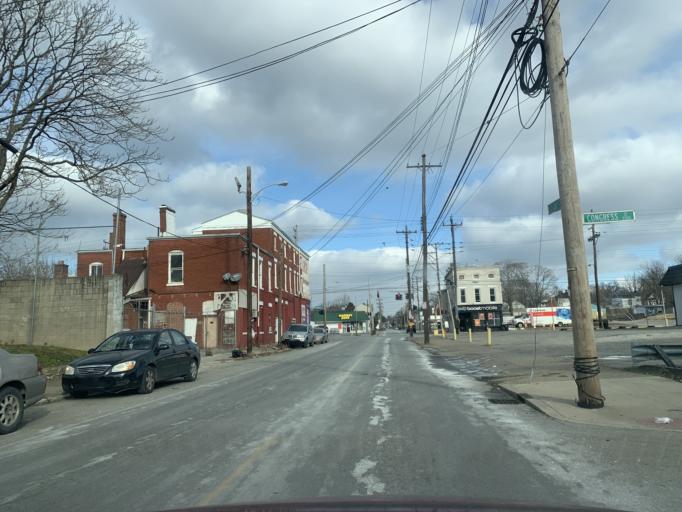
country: US
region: Kentucky
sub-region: Jefferson County
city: Louisville
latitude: 38.2588
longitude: -85.7938
